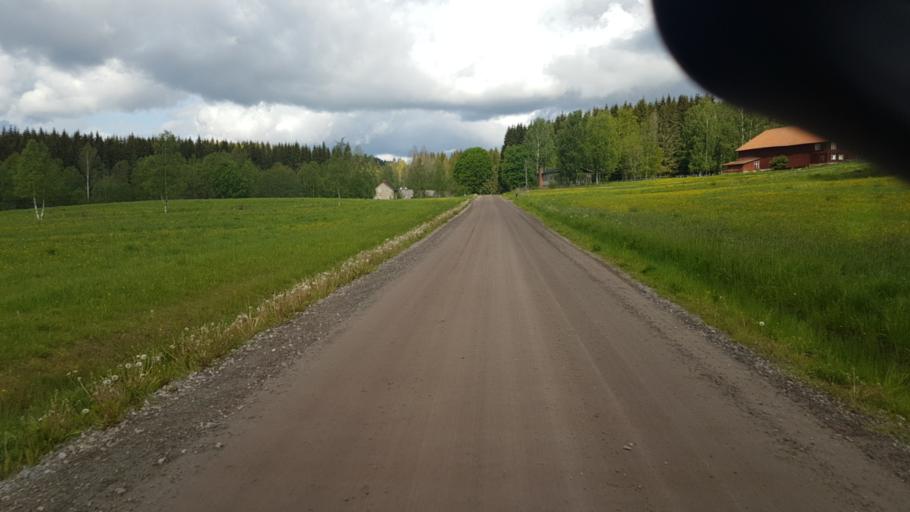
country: NO
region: Ostfold
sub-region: Romskog
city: Romskog
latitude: 59.6992
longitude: 12.0656
